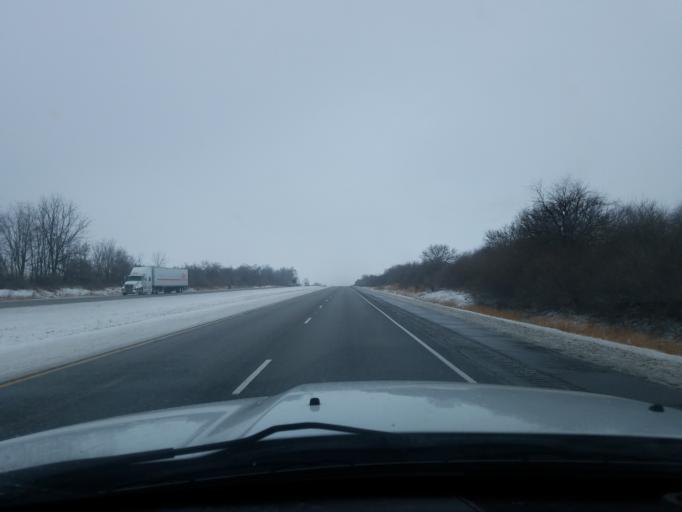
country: US
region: Indiana
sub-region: Fulton County
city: Rochester
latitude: 40.9665
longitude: -86.1681
